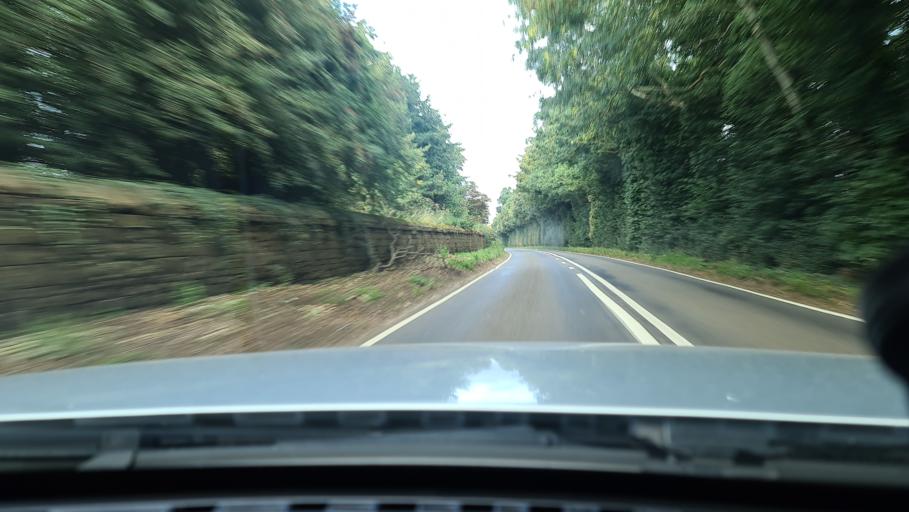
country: GB
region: England
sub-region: Oxfordshire
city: Hanwell
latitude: 52.0748
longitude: -1.3864
